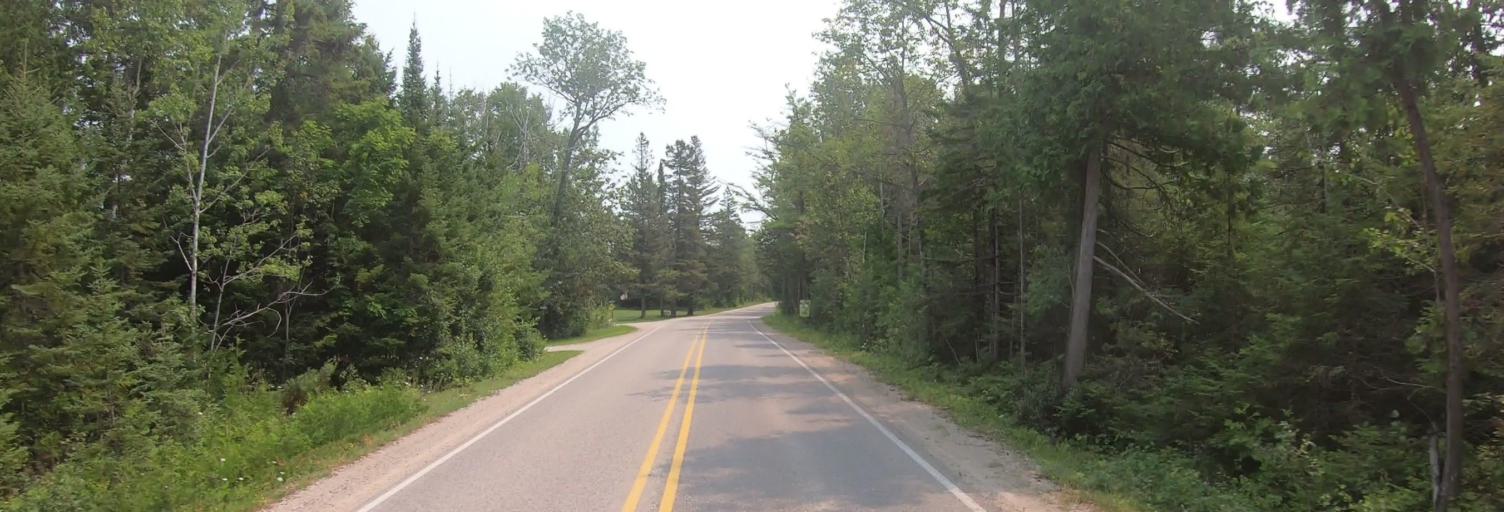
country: CA
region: Ontario
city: Thessalon
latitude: 45.9685
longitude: -83.6415
